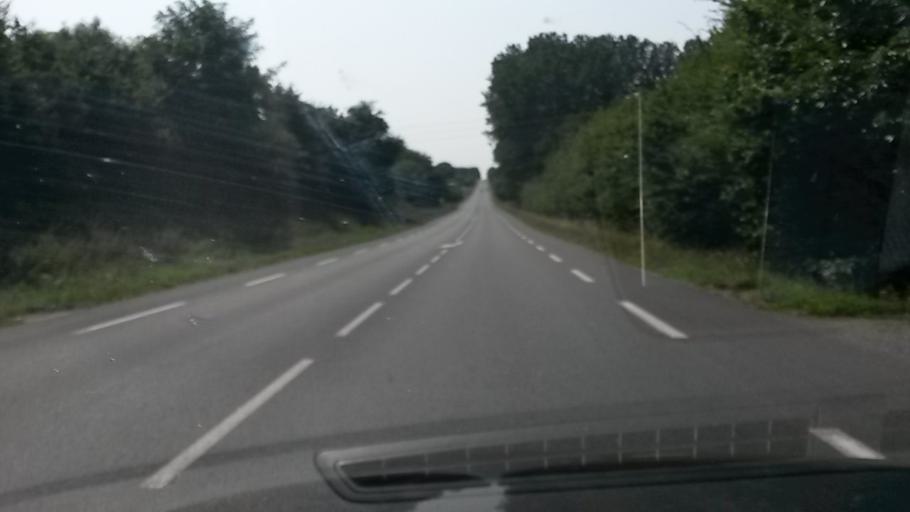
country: FR
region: Pays de la Loire
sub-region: Departement de la Mayenne
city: Saint-Fort
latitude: 47.8087
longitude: -0.7392
